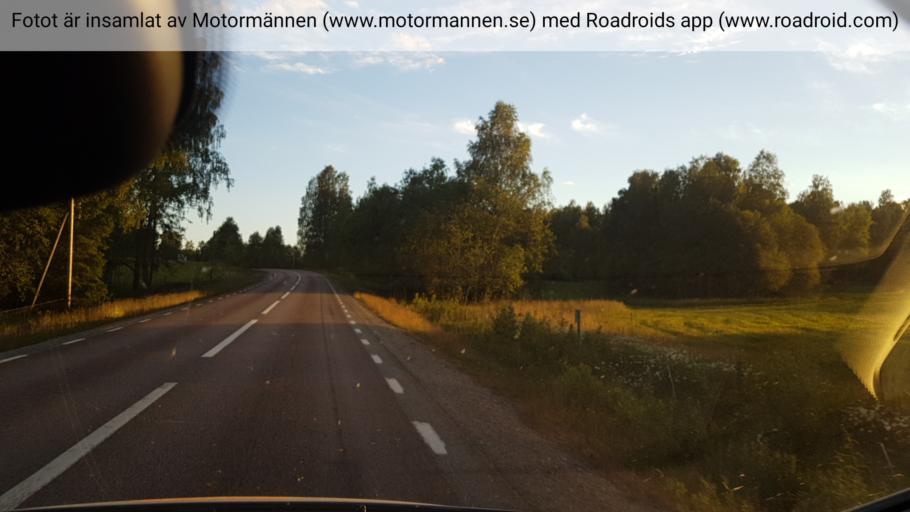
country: SE
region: Vaermland
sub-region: Sunne Kommun
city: Sunne
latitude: 59.6763
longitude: 13.0338
